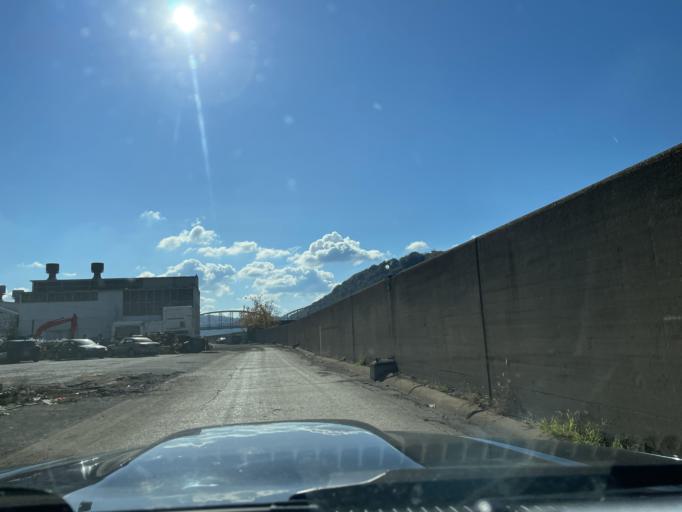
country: US
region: Pennsylvania
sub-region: Westmoreland County
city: New Kensington
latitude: 40.5683
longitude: -79.7722
